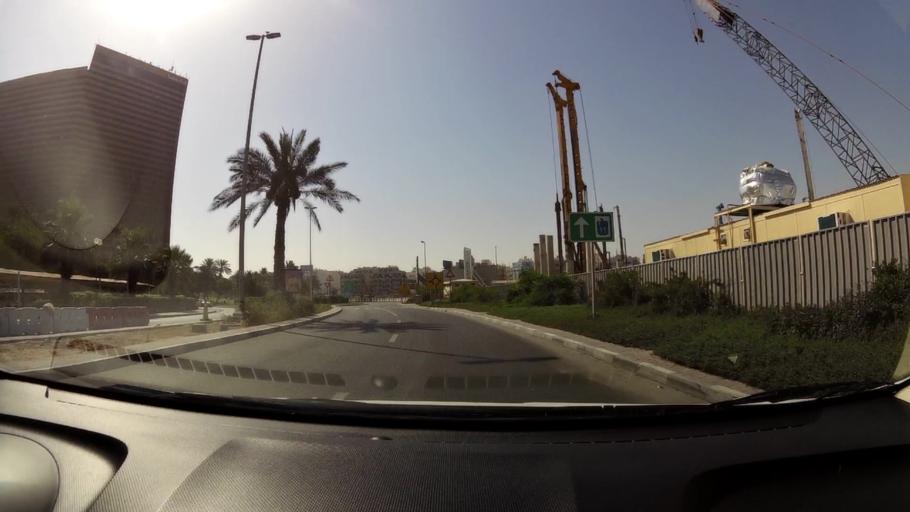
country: AE
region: Ash Shariqah
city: Sharjah
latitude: 25.2780
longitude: 55.3027
